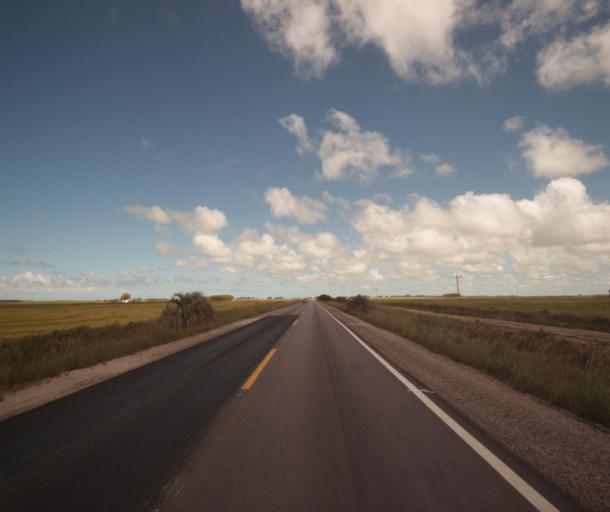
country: UY
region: Cerro Largo
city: Rio Branco
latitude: -32.8924
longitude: -52.7253
